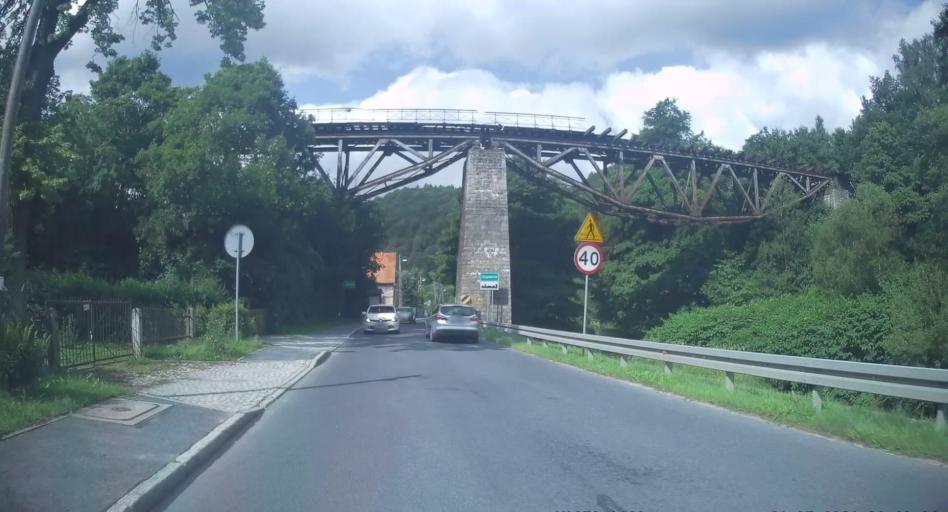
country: PL
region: Lower Silesian Voivodeship
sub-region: Powiat walbrzyski
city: Walim
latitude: 50.7403
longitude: 16.4092
